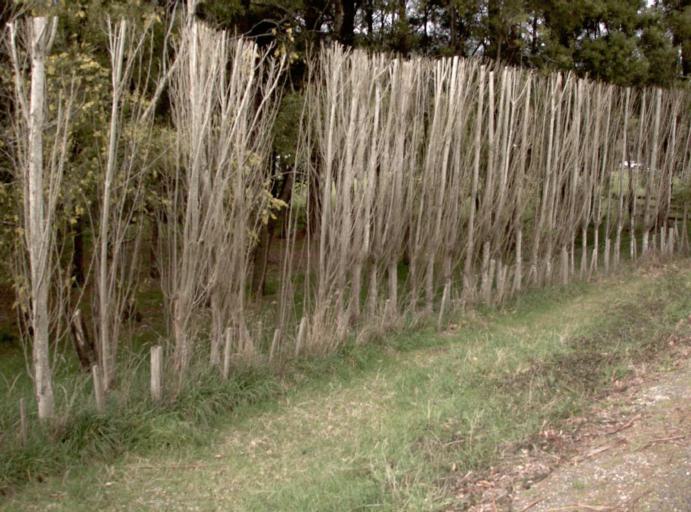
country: AU
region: Tasmania
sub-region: Launceston
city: Mayfield
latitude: -41.2622
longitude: 147.1598
